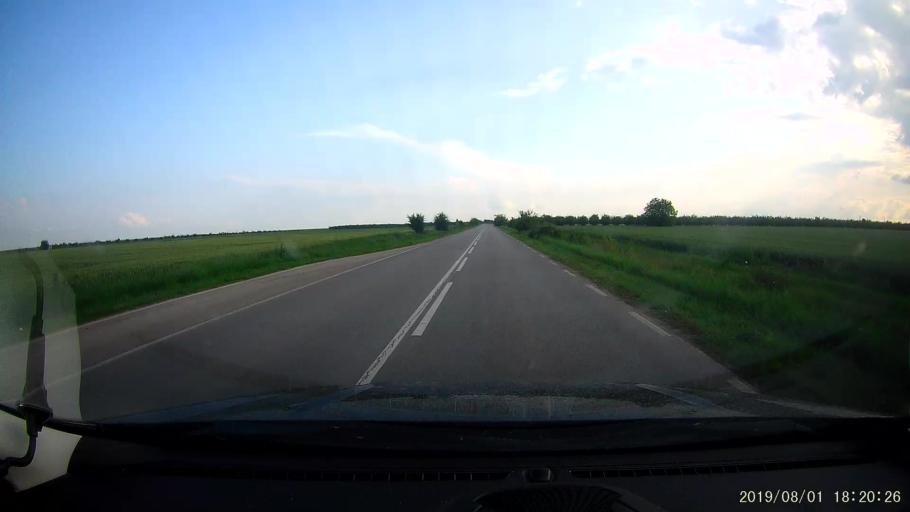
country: BG
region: Shumen
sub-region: Obshtina Kaolinovo
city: Kaolinovo
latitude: 43.6713
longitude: 27.0887
